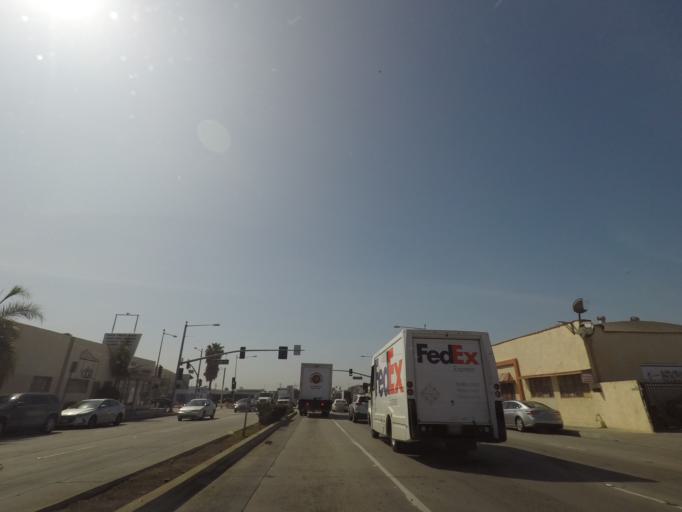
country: US
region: California
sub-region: Los Angeles County
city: Hawthorne
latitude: 33.9242
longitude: -118.3439
